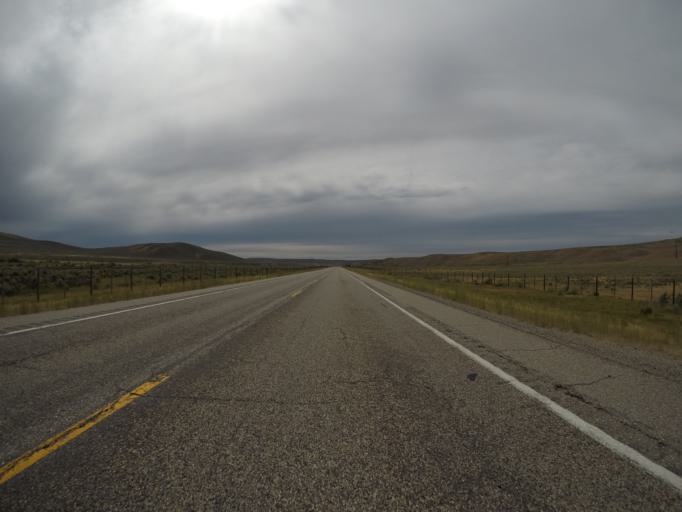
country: US
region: Utah
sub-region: Rich County
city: Randolph
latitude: 41.8228
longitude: -110.8947
